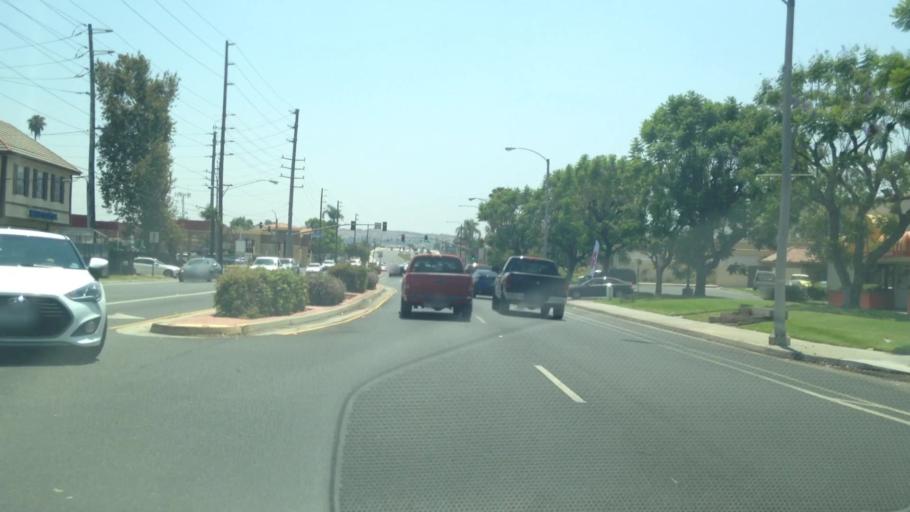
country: US
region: California
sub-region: Riverside County
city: Home Gardens
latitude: 33.9047
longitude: -117.4773
